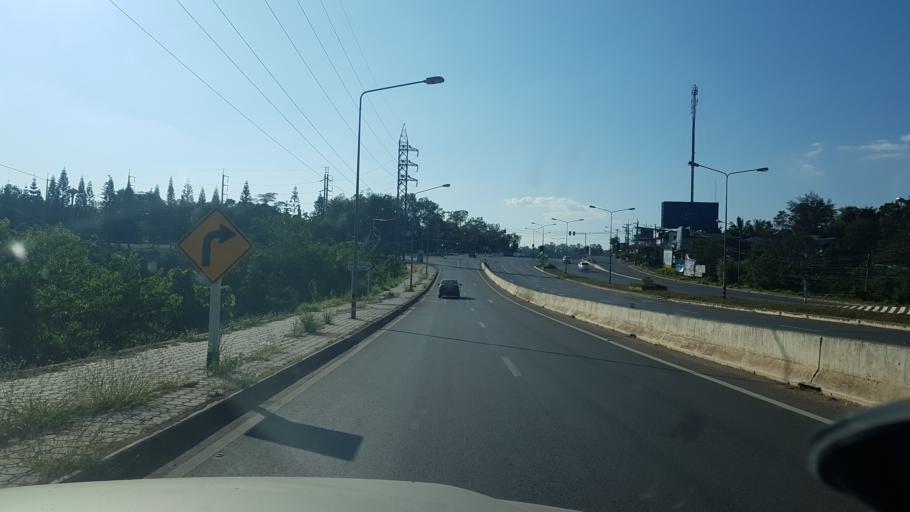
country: TH
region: Phetchabun
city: Khao Kho
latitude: 16.7688
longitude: 101.0276
